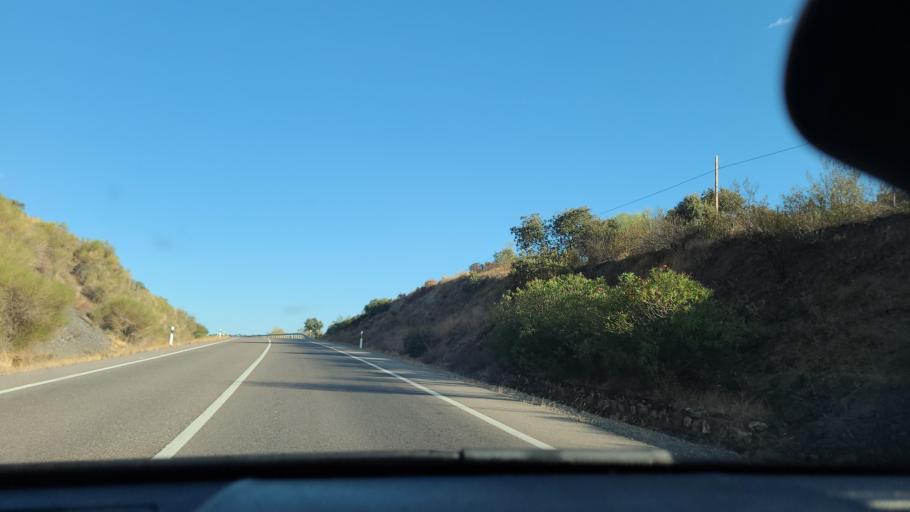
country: ES
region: Andalusia
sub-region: Province of Cordoba
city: Espiel
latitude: 38.1939
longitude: -5.0980
